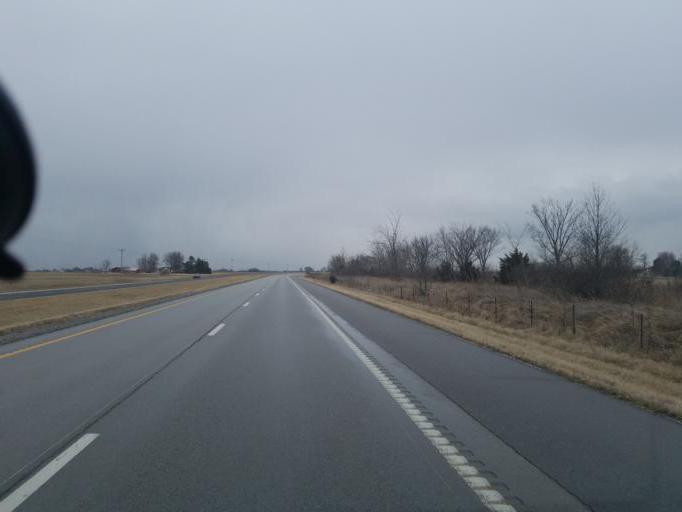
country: US
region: Missouri
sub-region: Macon County
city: Macon
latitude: 39.8350
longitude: -92.4768
